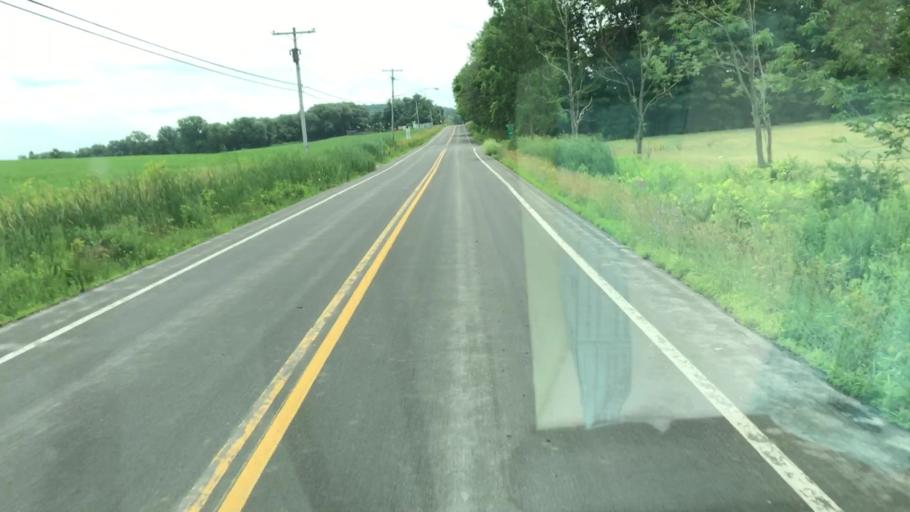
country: US
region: New York
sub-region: Onondaga County
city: Manlius
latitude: 42.9286
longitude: -75.9764
